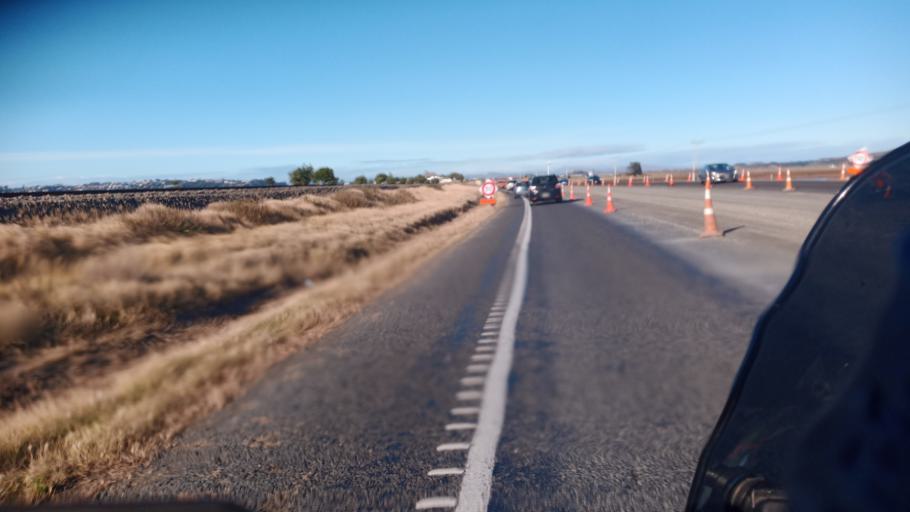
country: NZ
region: Hawke's Bay
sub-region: Napier City
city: Napier
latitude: -39.4538
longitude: 176.8717
